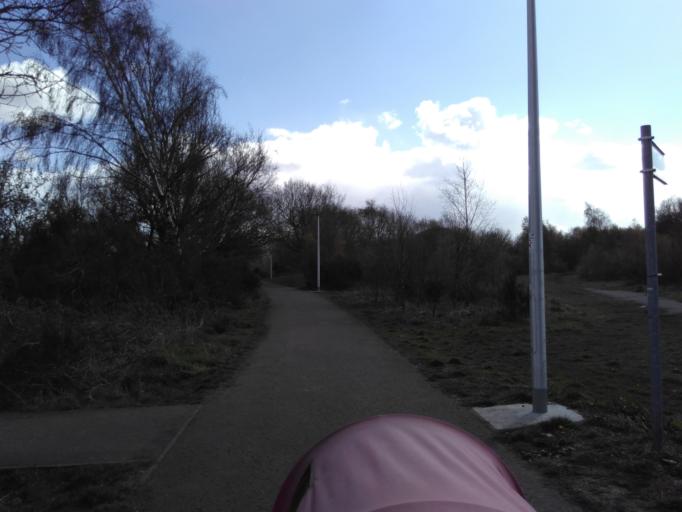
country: GB
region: Scotland
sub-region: Midlothian
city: Loanhead
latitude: 55.8730
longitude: -3.1508
